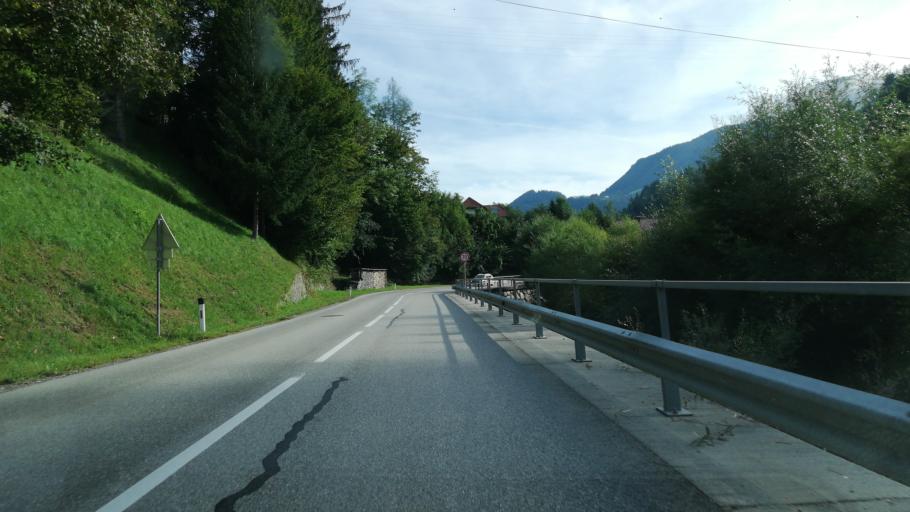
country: AT
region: Upper Austria
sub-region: Politischer Bezirk Steyr-Land
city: Maria Neustift
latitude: 47.8973
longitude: 14.5470
